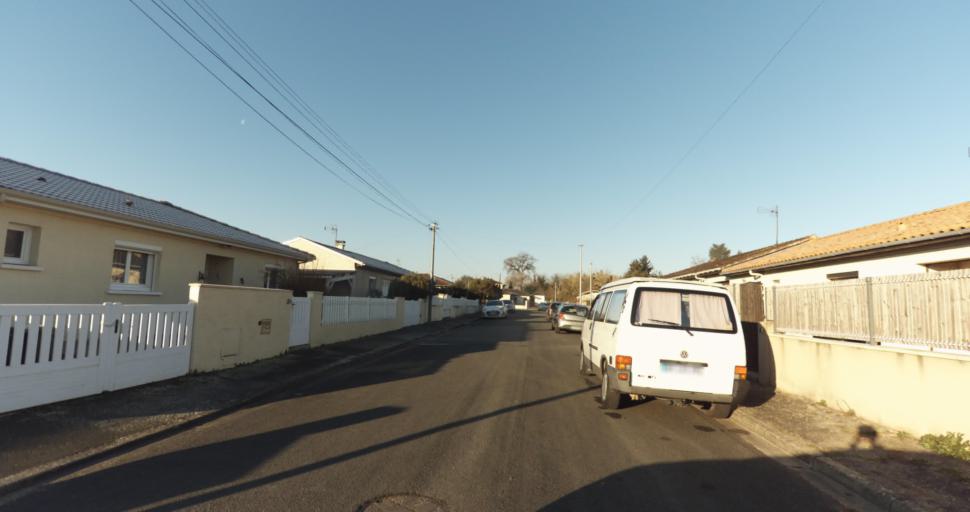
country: FR
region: Aquitaine
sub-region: Departement de la Gironde
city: Carbon-Blanc
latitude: 44.9069
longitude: -0.4967
